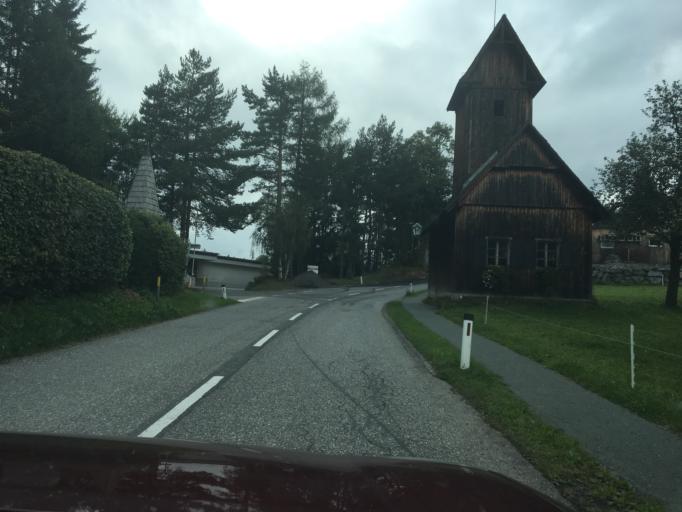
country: AT
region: Styria
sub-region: Politischer Bezirk Deutschlandsberg
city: Trahutten
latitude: 46.8230
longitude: 15.1524
